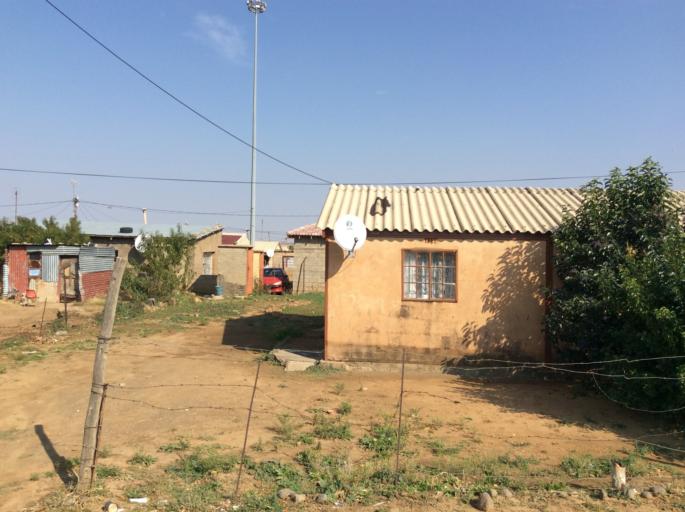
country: LS
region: Mafeteng
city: Mafeteng
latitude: -29.7173
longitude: 27.0295
